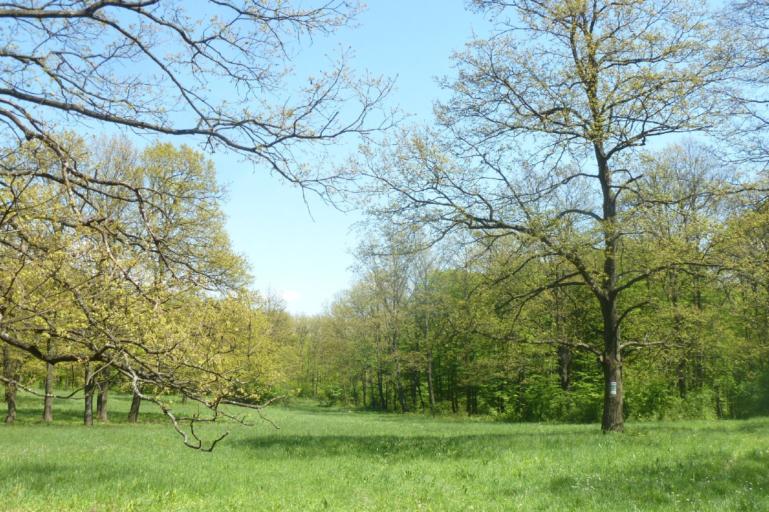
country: HU
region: Pest
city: Szob
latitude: 47.8795
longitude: 18.8280
